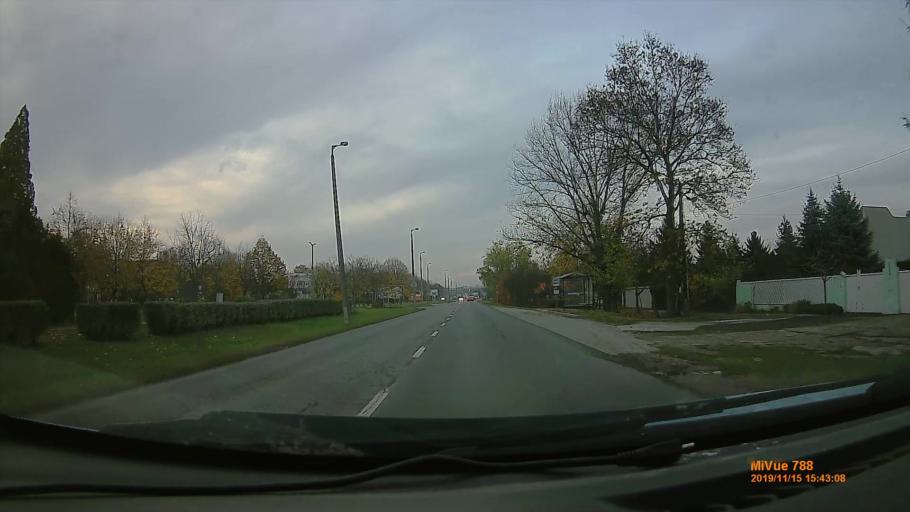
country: HU
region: Bekes
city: Bekescsaba
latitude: 46.6798
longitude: 21.1191
